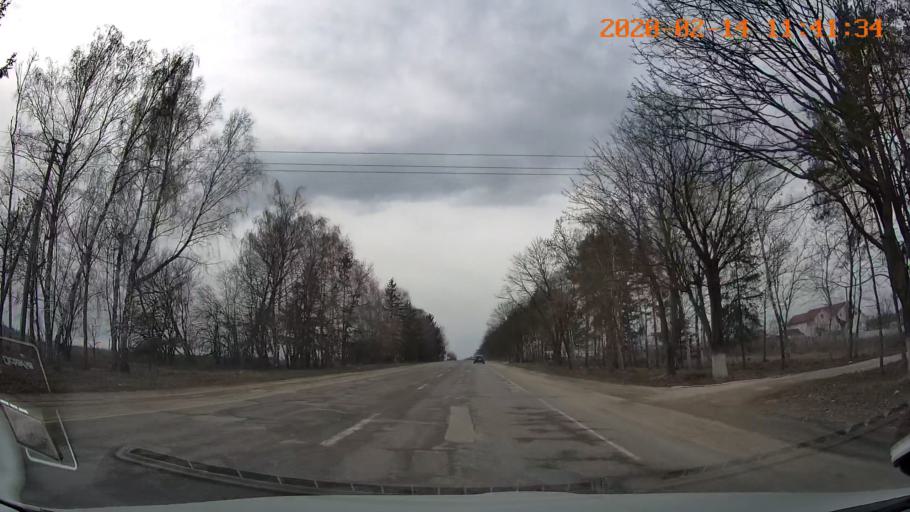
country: MD
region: Briceni
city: Briceni
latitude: 48.3489
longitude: 27.0795
